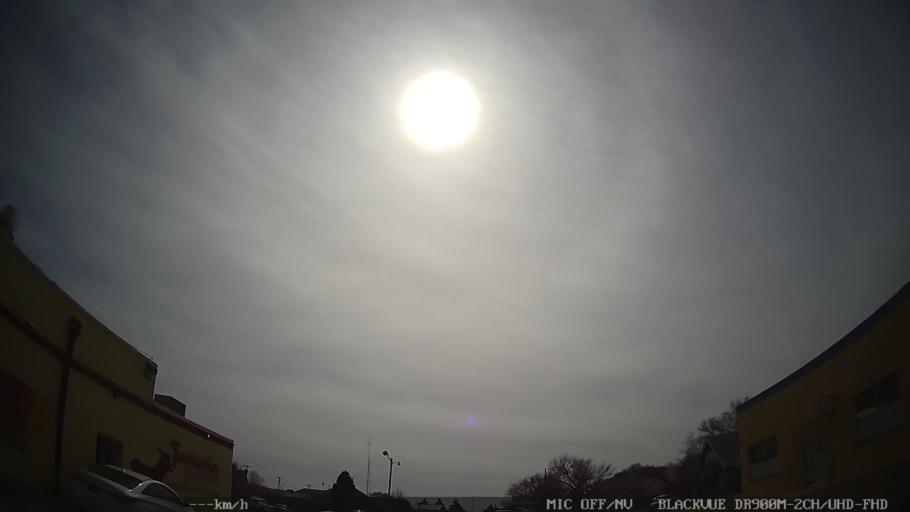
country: US
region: New Mexico
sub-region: Curry County
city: Clovis
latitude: 34.3895
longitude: -103.2114
